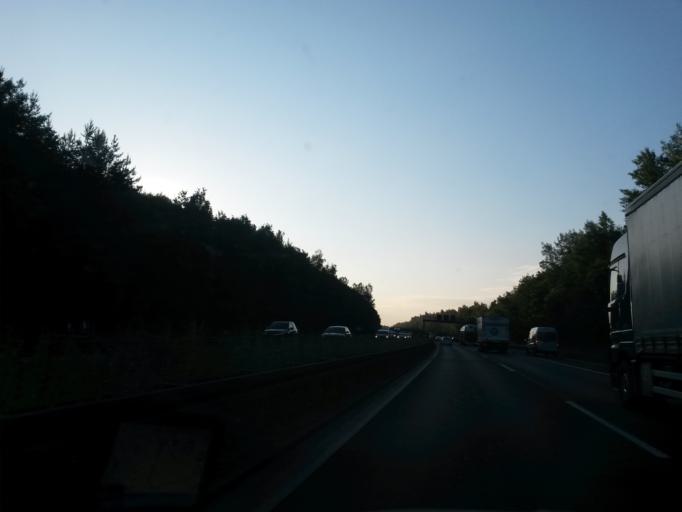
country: DE
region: Bavaria
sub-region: Regierungsbezirk Mittelfranken
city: Nuernberg
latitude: 49.3945
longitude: 11.0871
